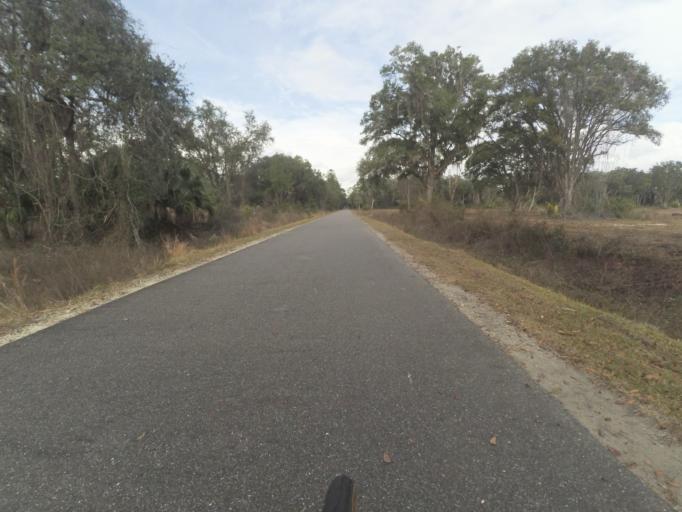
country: US
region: Florida
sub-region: Alachua County
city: Gainesville
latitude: 29.6263
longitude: -82.3108
